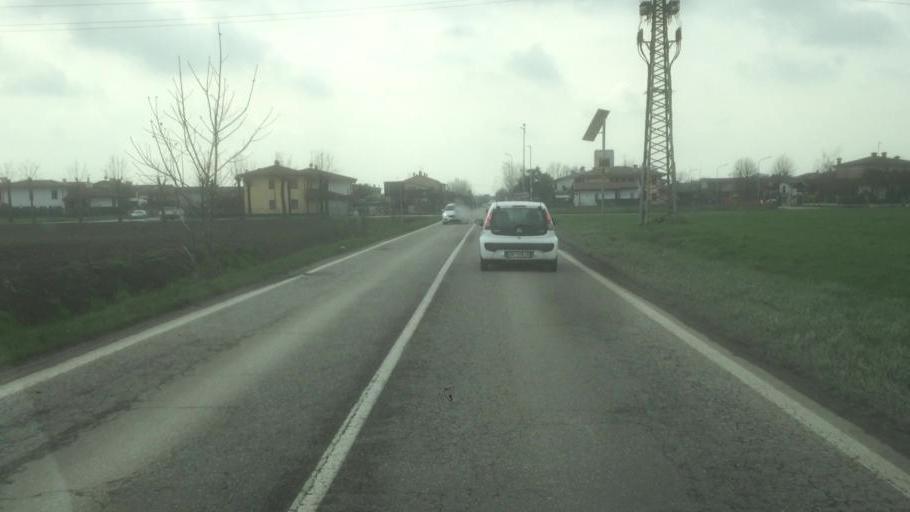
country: IT
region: Lombardy
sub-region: Provincia di Mantova
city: Casaloldo
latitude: 45.2600
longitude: 10.4766
